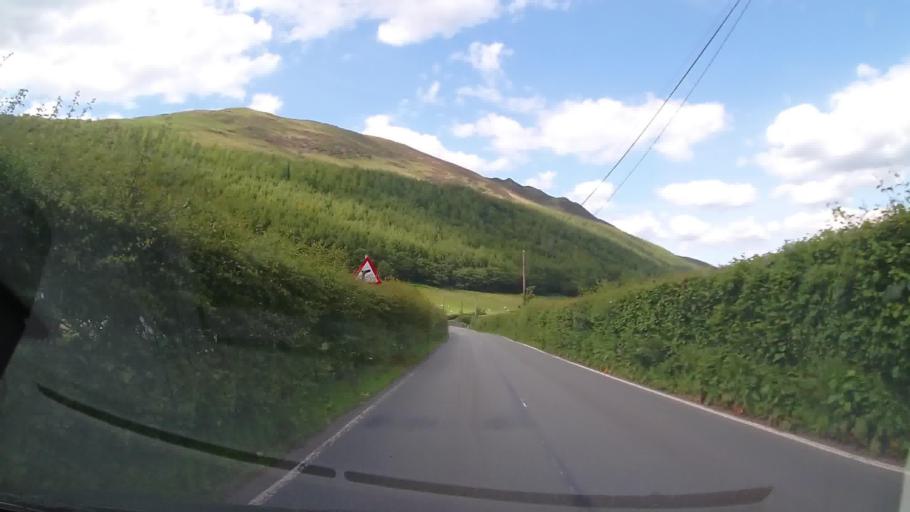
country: GB
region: Wales
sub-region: Gwynedd
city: Corris
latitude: 52.6540
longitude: -3.9343
